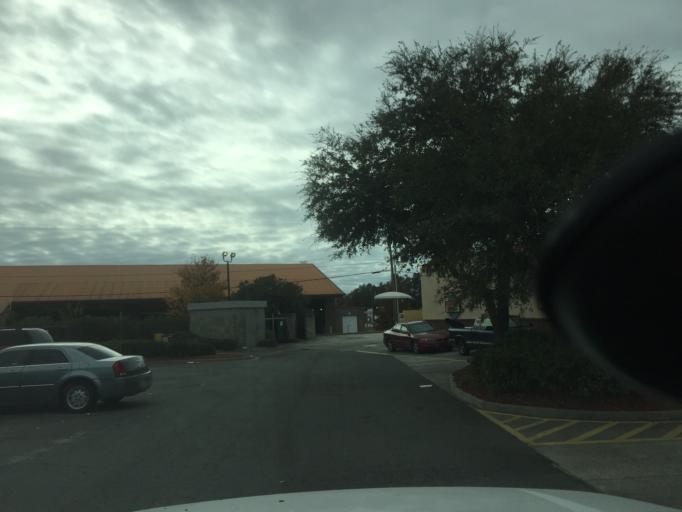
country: US
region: Georgia
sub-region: Chatham County
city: Garden City
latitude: 32.1260
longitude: -81.1689
